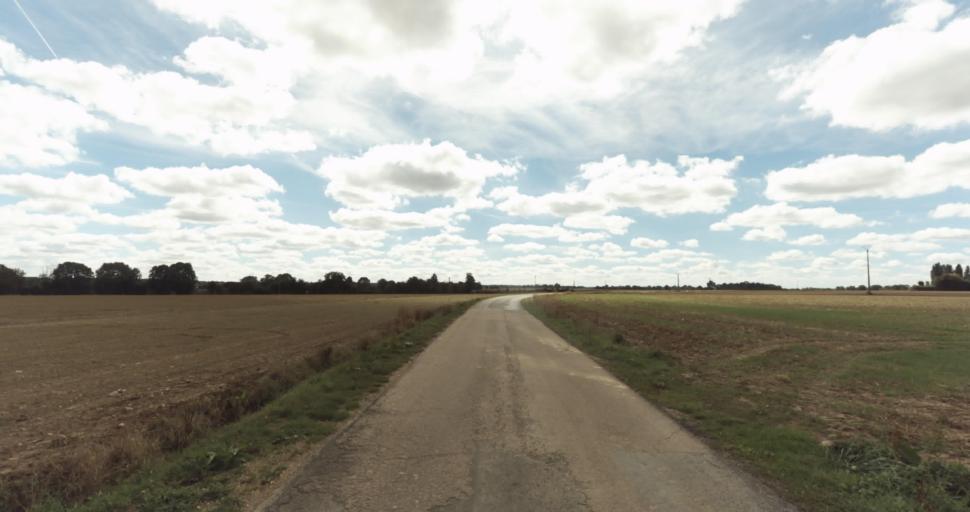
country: FR
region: Lower Normandy
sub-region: Departement du Calvados
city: Orbec
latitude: 48.9156
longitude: 0.3724
